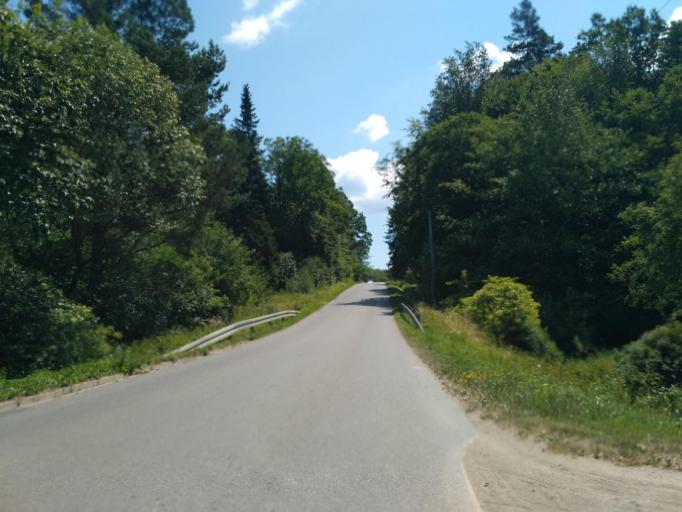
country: PL
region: Subcarpathian Voivodeship
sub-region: Powiat sanocki
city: Niebieszczany
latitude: 49.4901
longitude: 22.1827
